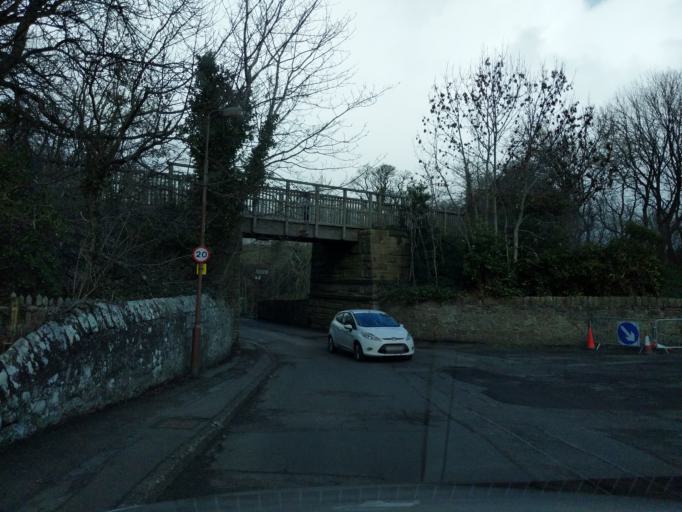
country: GB
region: Scotland
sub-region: Edinburgh
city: Currie
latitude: 55.8954
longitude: -3.3086
